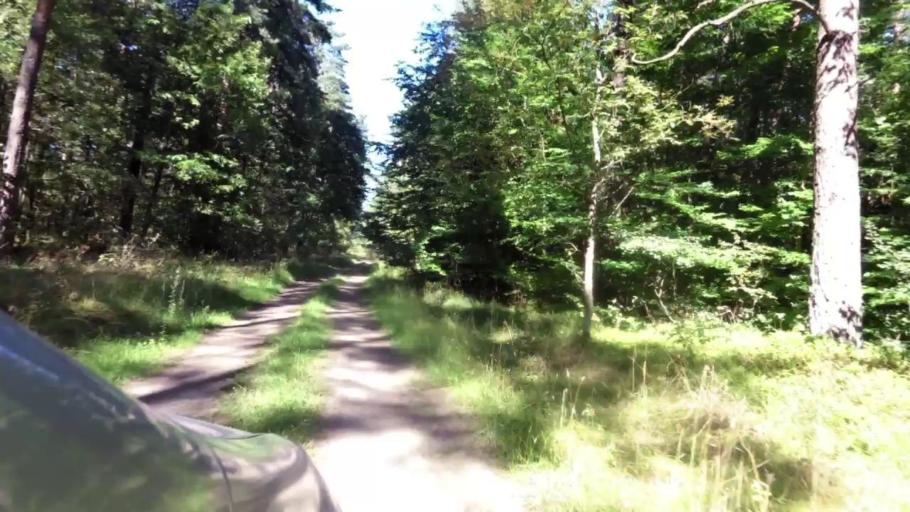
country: PL
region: West Pomeranian Voivodeship
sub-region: Powiat szczecinecki
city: Bialy Bor
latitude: 53.8300
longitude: 16.8695
